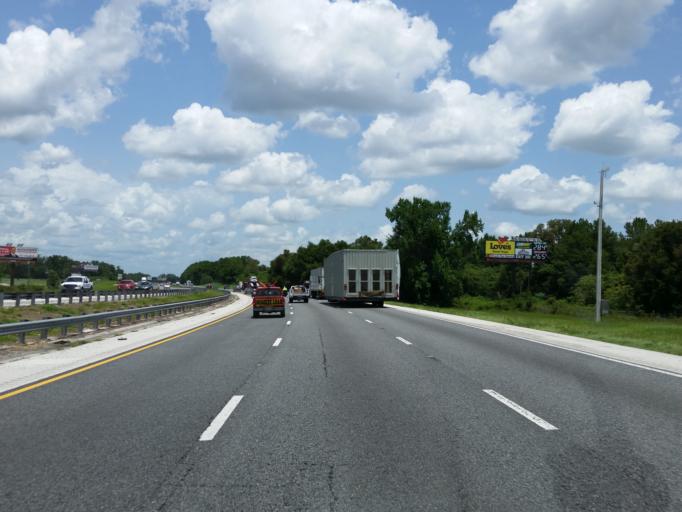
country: US
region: Florida
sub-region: Marion County
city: Ocala
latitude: 29.2259
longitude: -82.1847
